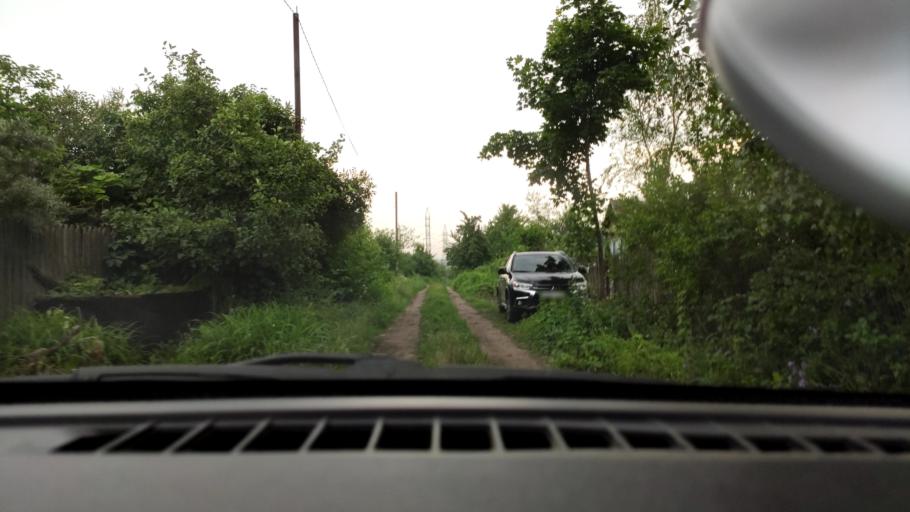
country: RU
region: Samara
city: Petra-Dubrava
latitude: 53.2643
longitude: 50.2938
